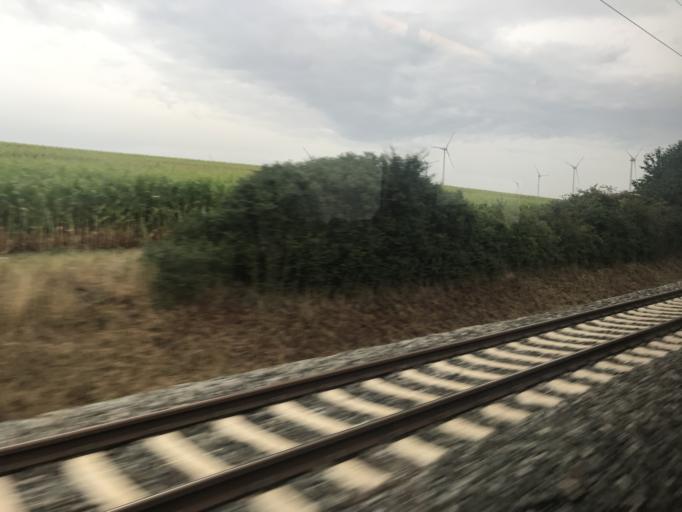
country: DE
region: Bavaria
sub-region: Regierungsbezirk Unterfranken
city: Bergtheim
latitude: 49.9384
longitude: 10.0865
